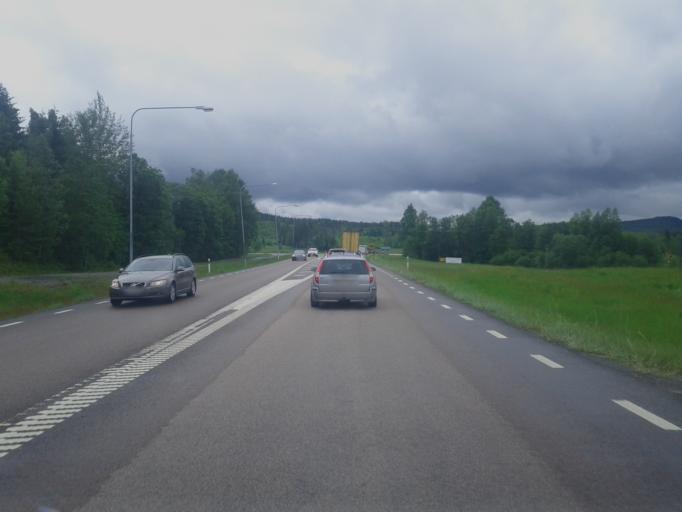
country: SE
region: Vaesternorrland
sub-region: Haernoesands Kommun
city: Haernoesand
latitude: 62.6657
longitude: 17.8479
